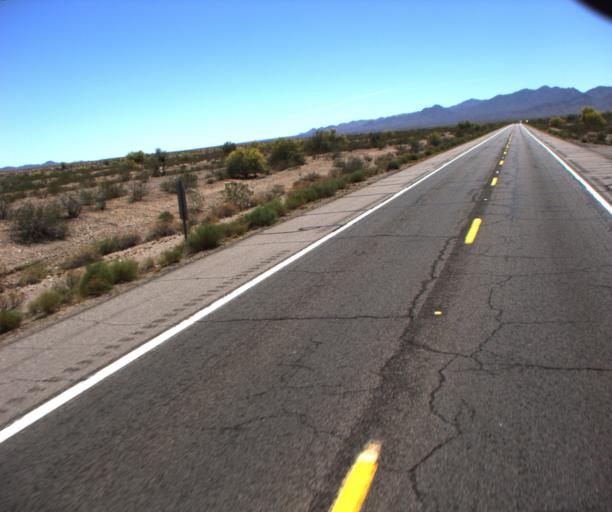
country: US
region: Arizona
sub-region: Mohave County
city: Desert Hills
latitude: 34.7165
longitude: -114.3097
